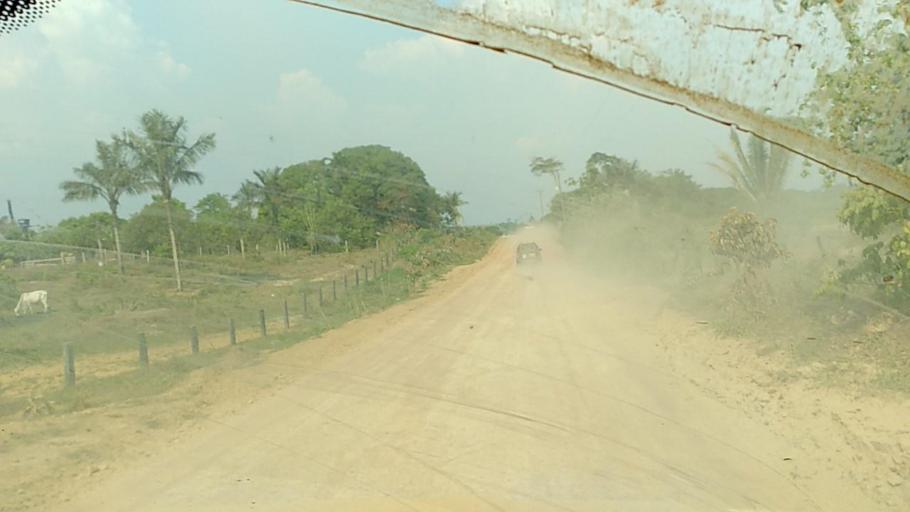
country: BR
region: Rondonia
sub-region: Porto Velho
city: Porto Velho
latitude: -8.6834
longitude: -63.1878
